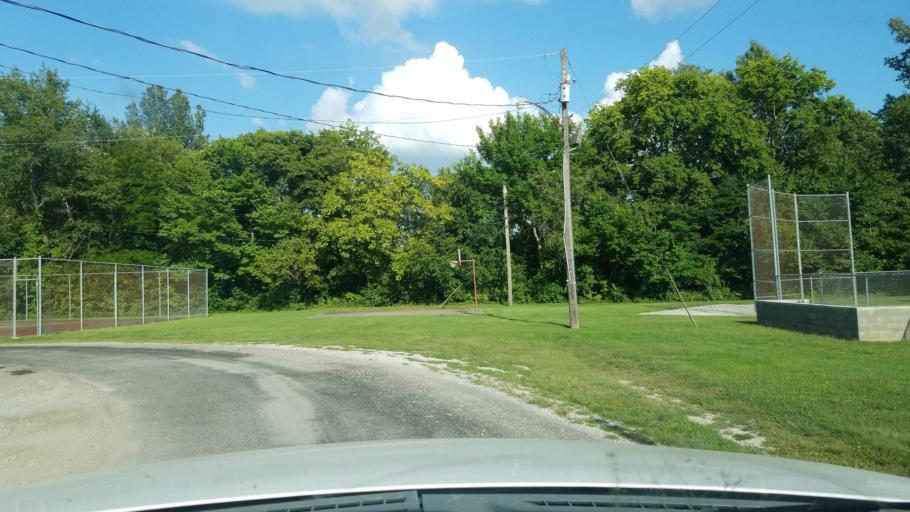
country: US
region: Illinois
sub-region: Saline County
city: Harrisburg
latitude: 37.8266
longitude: -88.5309
